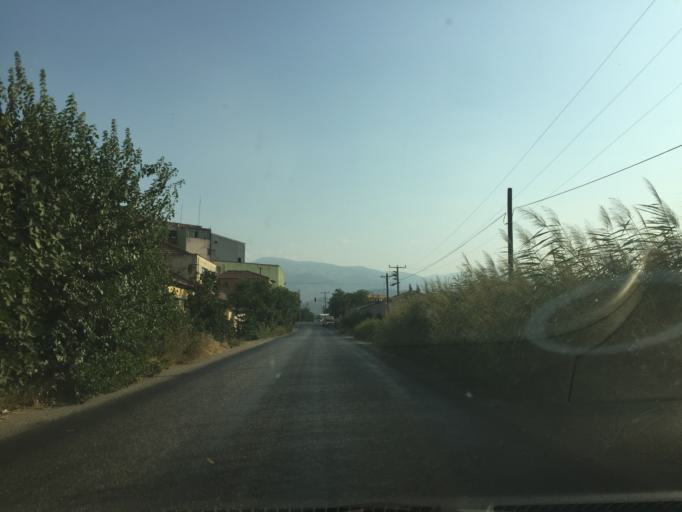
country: TR
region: Manisa
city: Salihli
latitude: 38.4966
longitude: 28.1822
